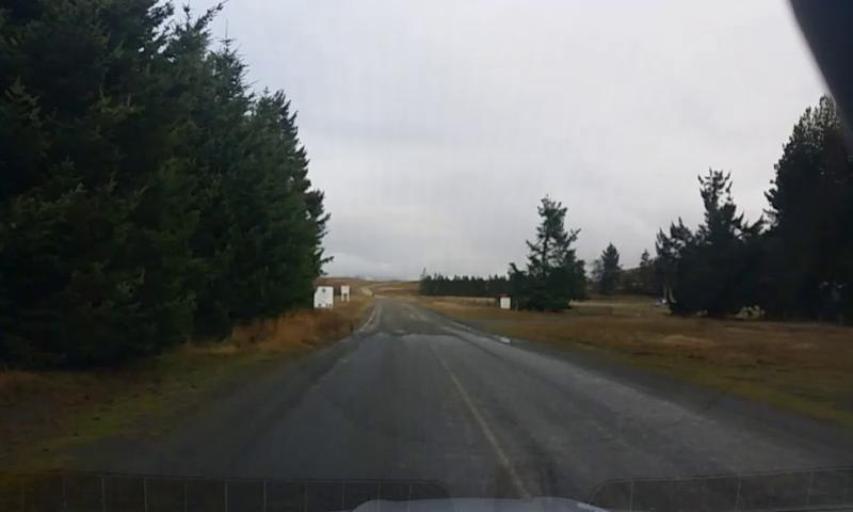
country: NZ
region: Canterbury
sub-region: Ashburton District
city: Methven
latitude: -43.6145
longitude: 171.1683
